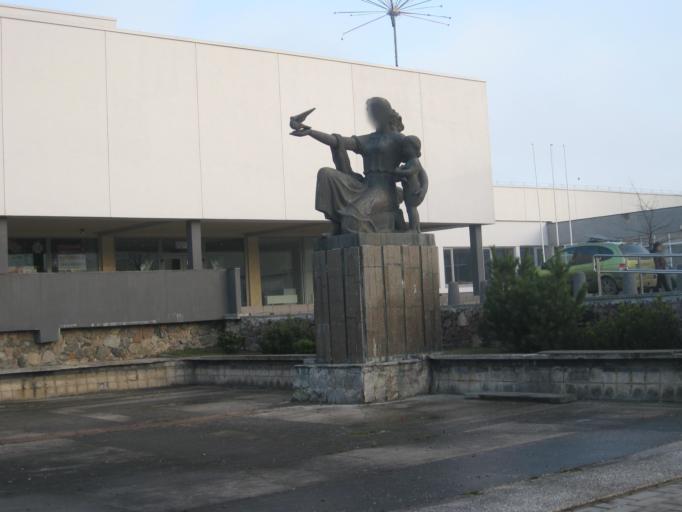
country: LT
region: Kauno apskritis
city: Dainava (Kaunas)
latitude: 54.9063
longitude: 23.9744
